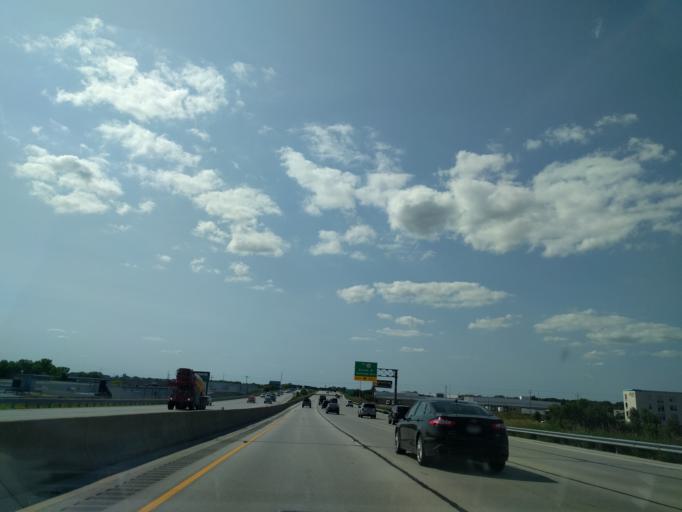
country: US
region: Wisconsin
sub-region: Brown County
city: Ashwaubenon
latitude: 44.4765
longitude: -88.0505
